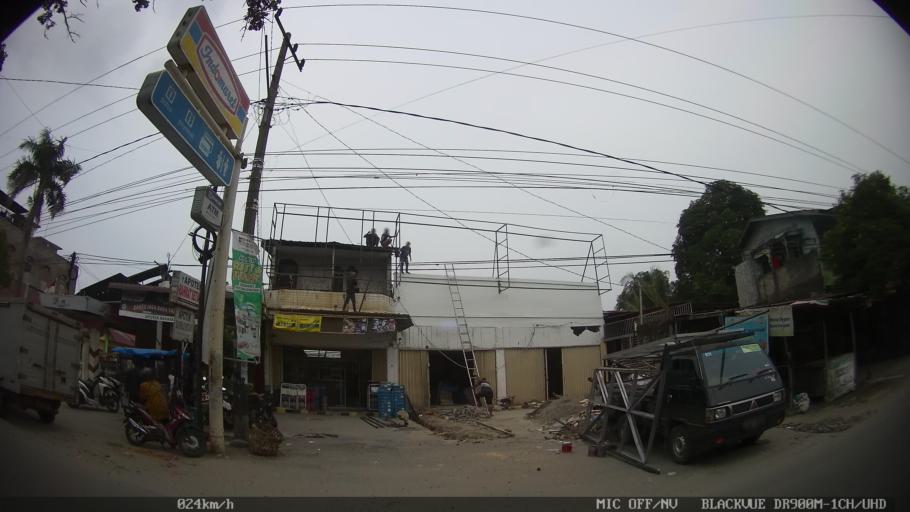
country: ID
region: North Sumatra
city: Medan
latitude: 3.5801
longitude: 98.7295
